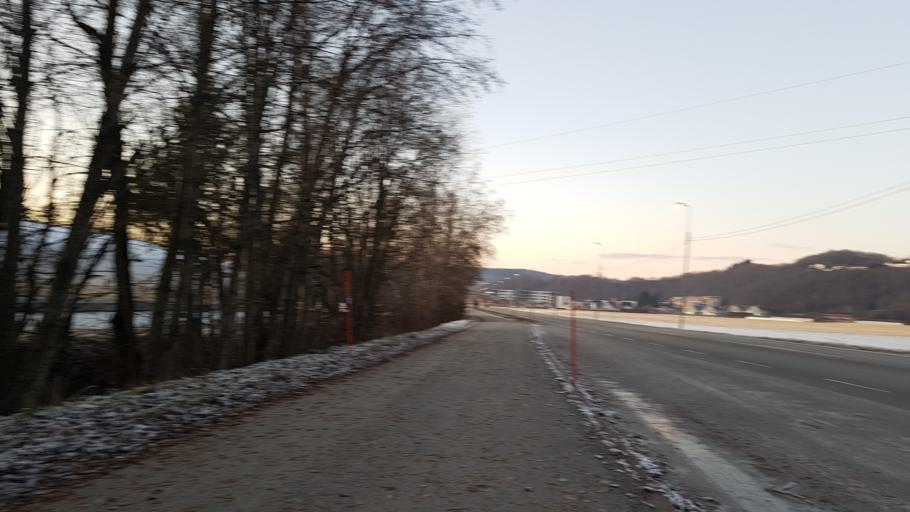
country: NO
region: Sor-Trondelag
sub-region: Melhus
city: Melhus
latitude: 63.2784
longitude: 10.2901
